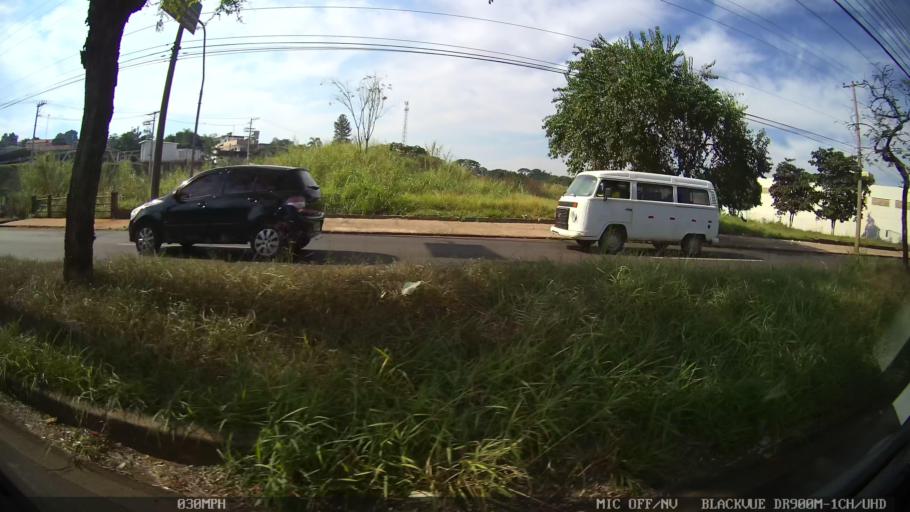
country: BR
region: Sao Paulo
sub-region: Araraquara
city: Araraquara
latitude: -21.8016
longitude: -48.1676
